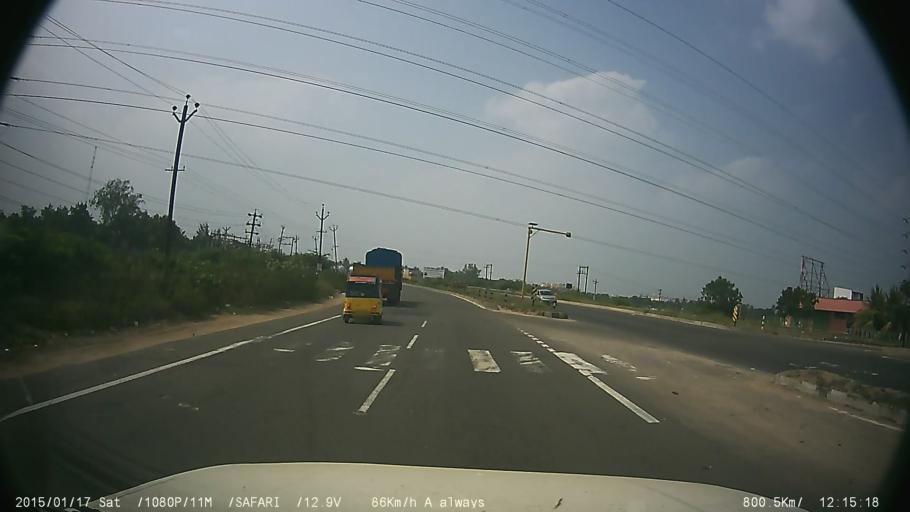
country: IN
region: Tamil Nadu
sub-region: Kancheepuram
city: Sriperumbudur
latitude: 12.9224
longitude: 79.8751
